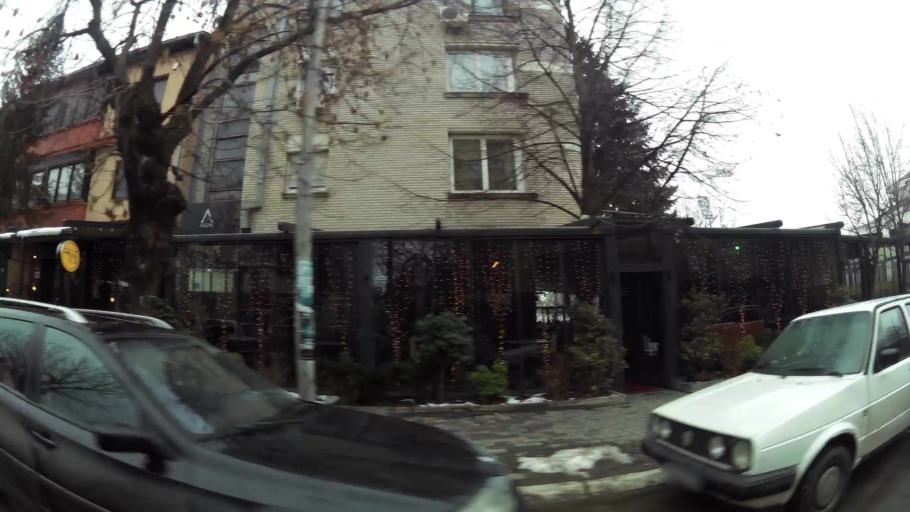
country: XK
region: Pristina
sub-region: Komuna e Prishtines
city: Pristina
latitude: 42.6642
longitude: 21.1591
